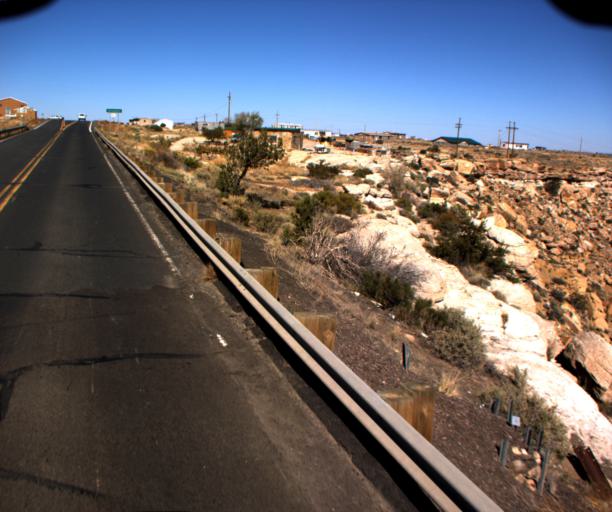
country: US
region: Arizona
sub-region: Navajo County
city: First Mesa
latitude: 35.8146
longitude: -110.5290
